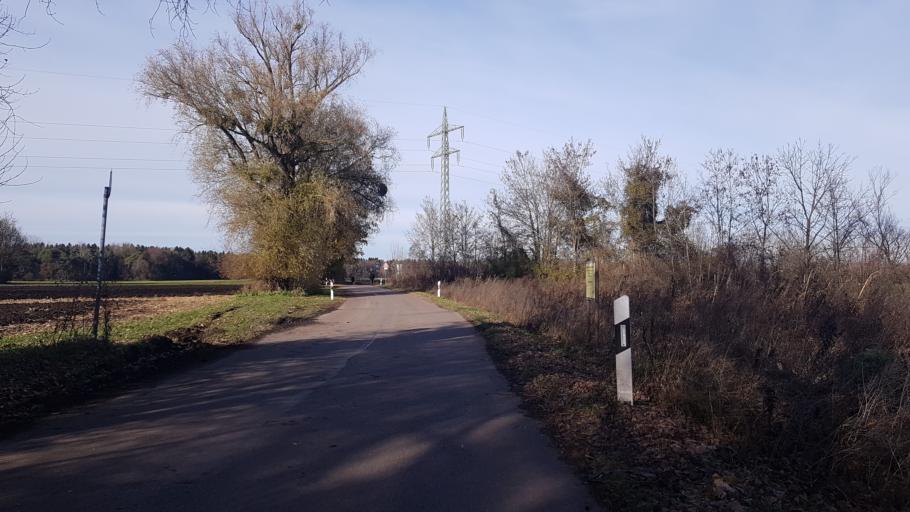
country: DE
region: Bavaria
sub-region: Upper Bavaria
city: Karlsfeld
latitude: 48.2352
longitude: 11.5041
